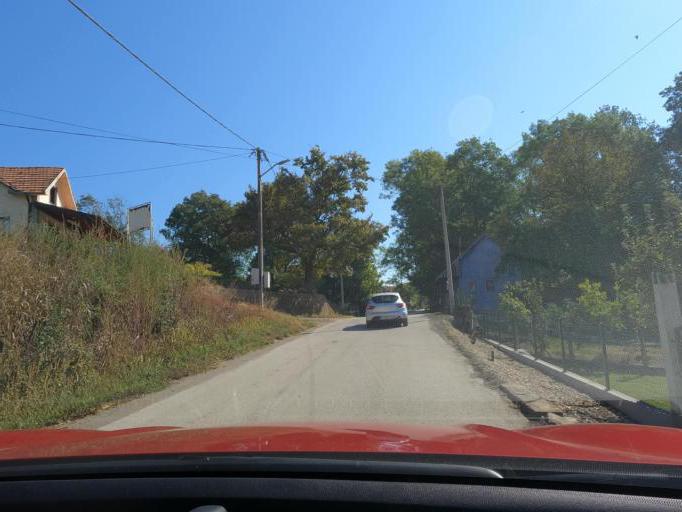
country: RS
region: Central Serbia
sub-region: Raski Okrug
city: Kraljevo
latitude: 43.7662
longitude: 20.6696
